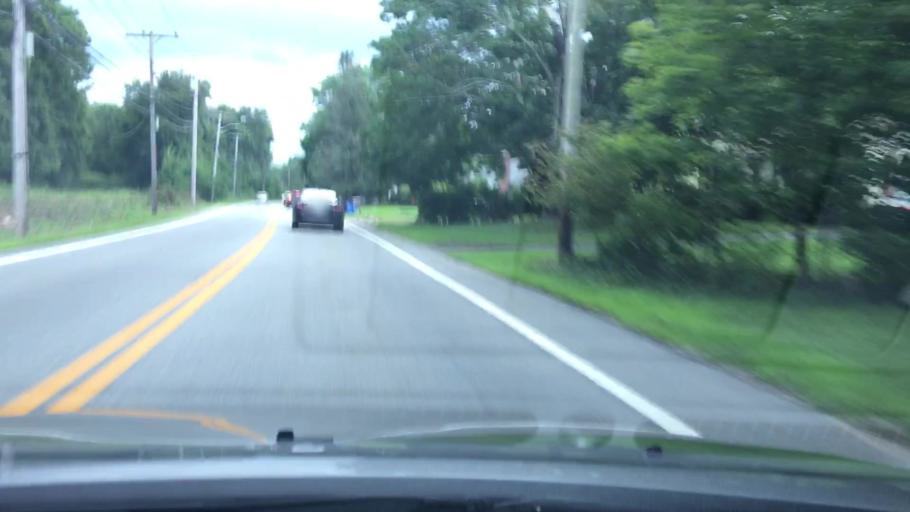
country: US
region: Rhode Island
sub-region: Providence County
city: Cumberland
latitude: 41.9933
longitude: -71.4146
